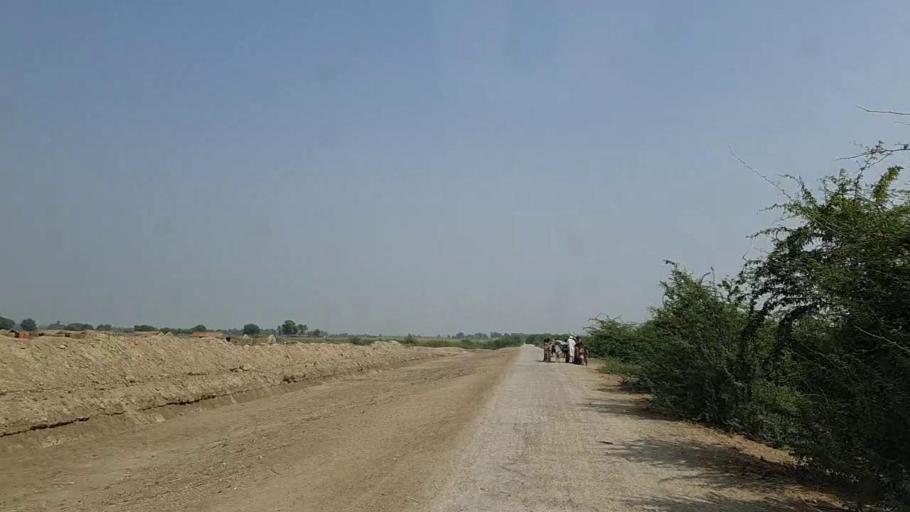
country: PK
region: Sindh
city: Naukot
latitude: 24.7836
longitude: 69.3521
